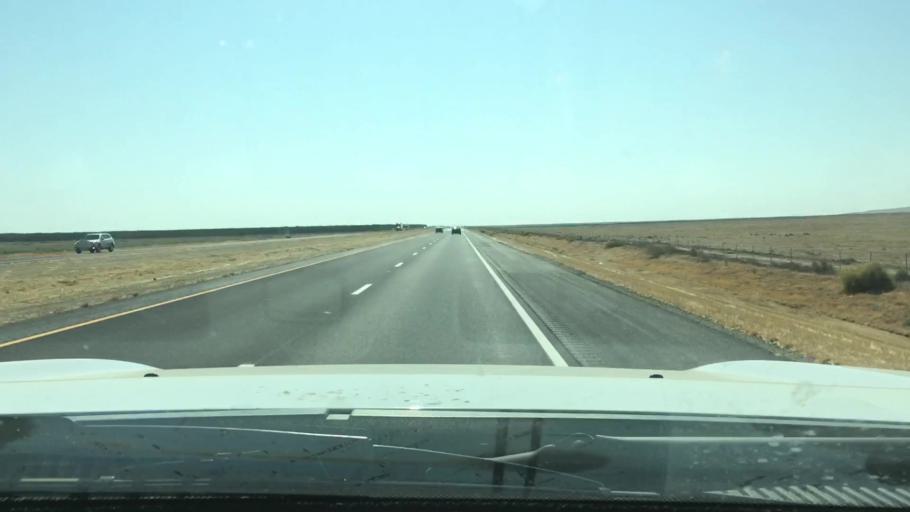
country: US
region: California
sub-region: Kern County
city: Lost Hills
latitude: 35.6227
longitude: -119.9828
